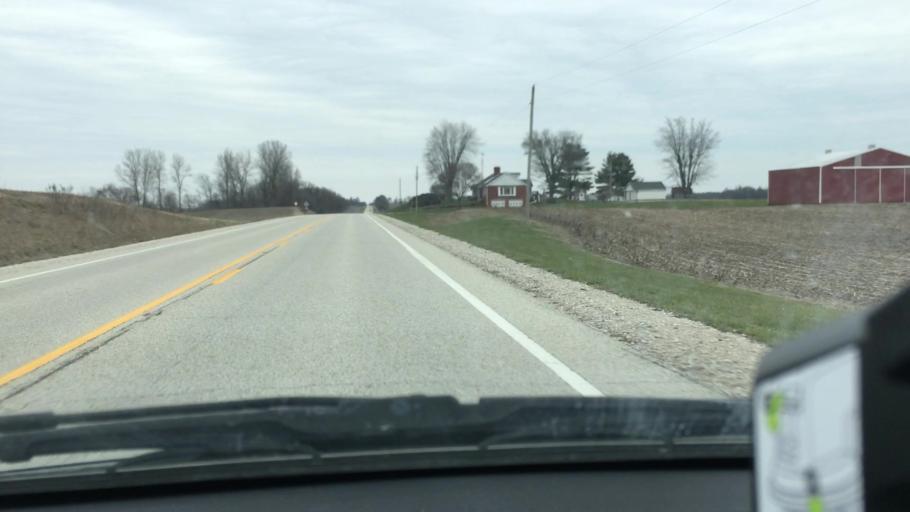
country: US
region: Indiana
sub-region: Daviess County
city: Odon
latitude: 38.9427
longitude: -87.0168
